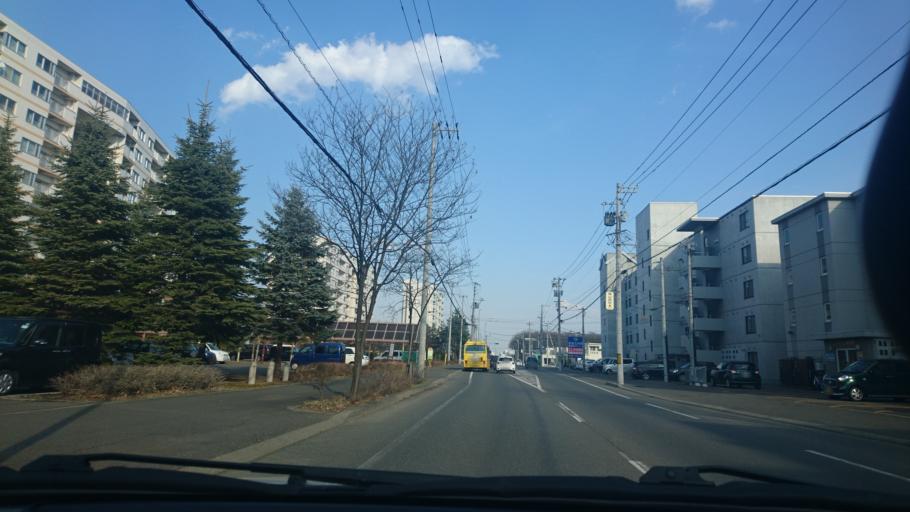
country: JP
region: Hokkaido
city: Obihiro
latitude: 42.9250
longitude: 143.1693
